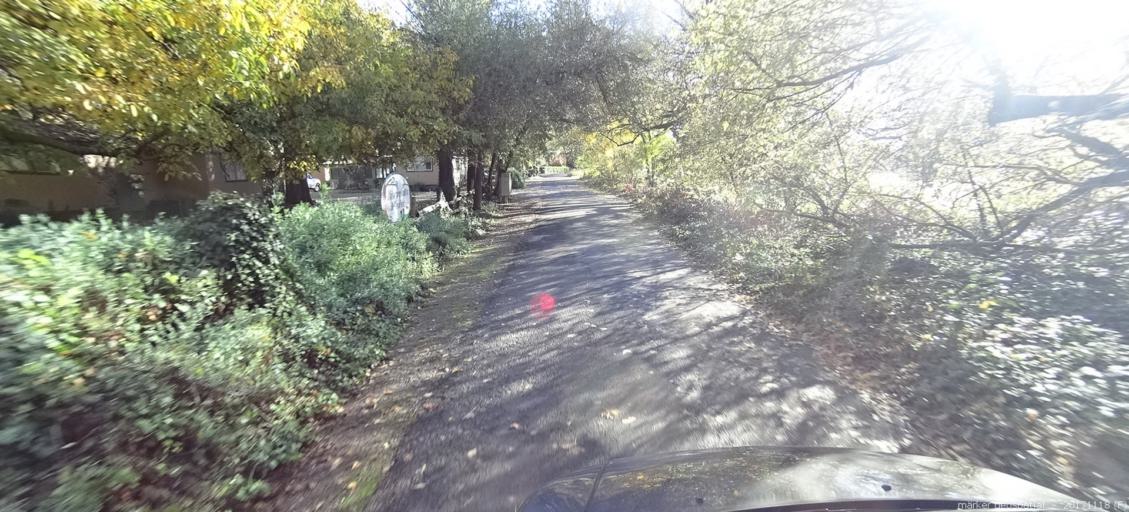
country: US
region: California
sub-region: Shasta County
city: Anderson
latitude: 40.4610
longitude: -122.2372
